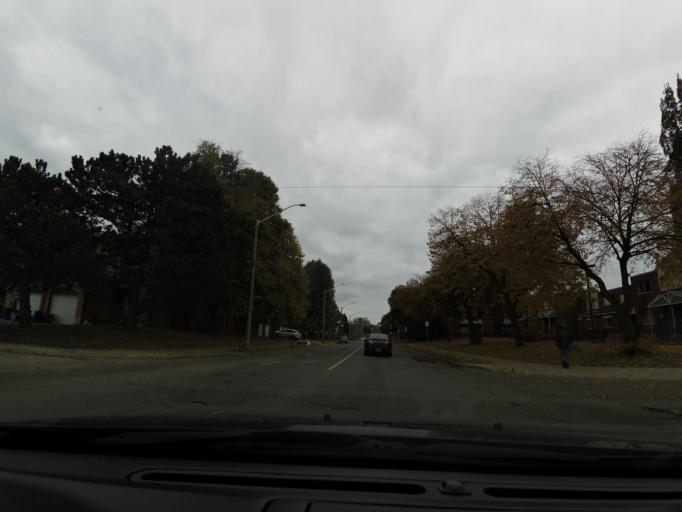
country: CA
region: Ontario
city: Hamilton
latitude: 43.2689
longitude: -79.8637
